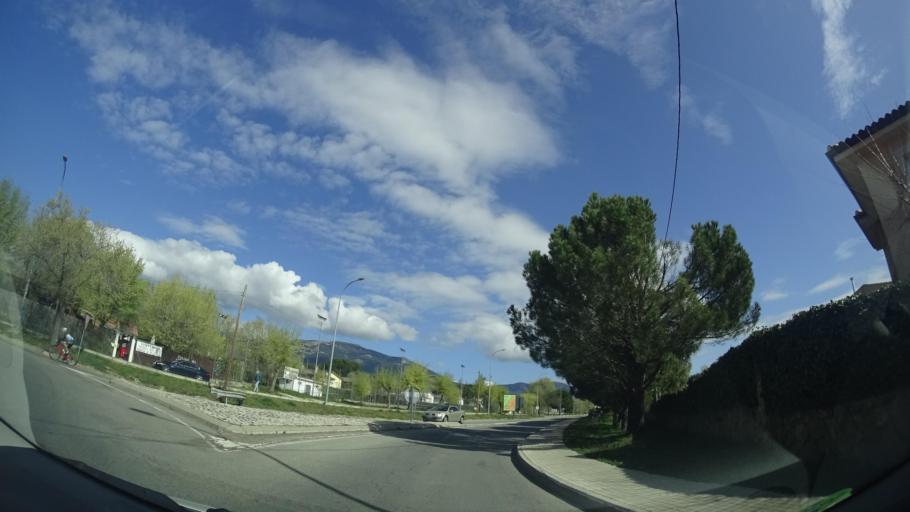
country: ES
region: Madrid
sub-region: Provincia de Madrid
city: Miraflores de la Sierra
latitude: 40.7568
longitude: -3.7828
